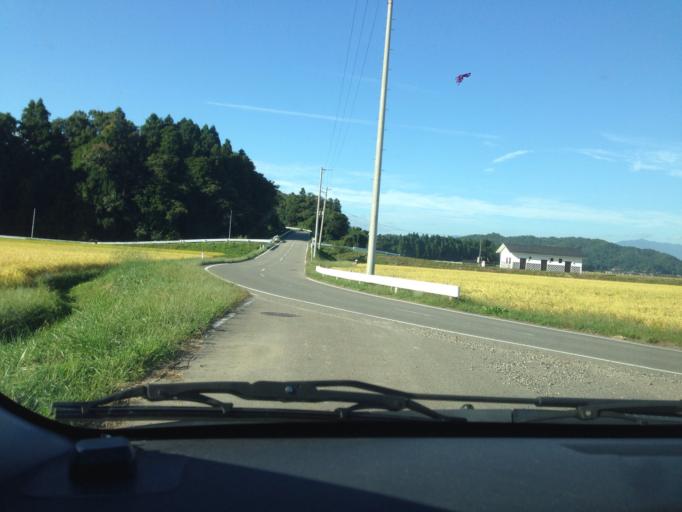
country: JP
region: Fukushima
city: Kitakata
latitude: 37.5901
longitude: 139.8133
